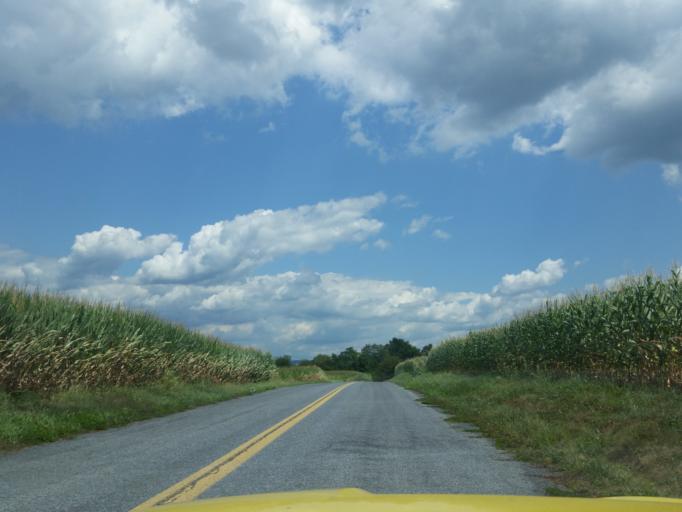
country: US
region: Pennsylvania
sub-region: Lebanon County
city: Palmyra
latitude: 40.4022
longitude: -76.6047
